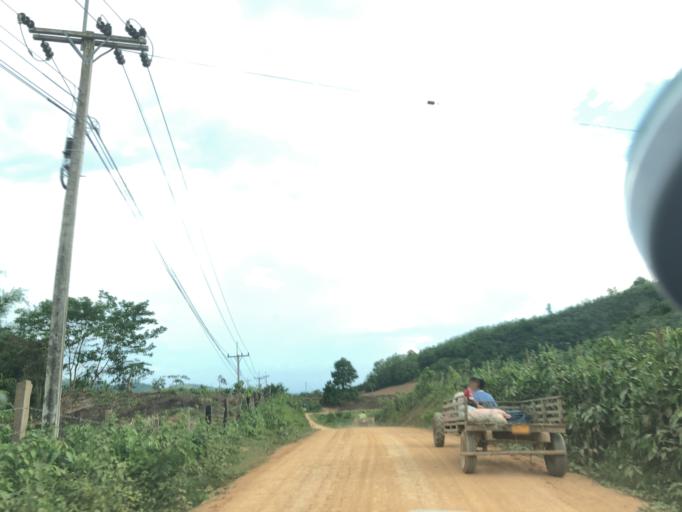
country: TH
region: Loei
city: Chiang Khan
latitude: 17.9981
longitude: 101.4193
